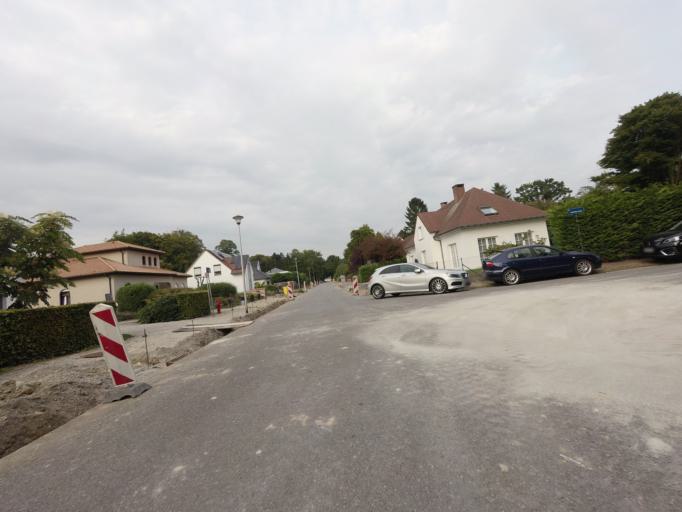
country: BE
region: Flanders
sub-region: Provincie Vlaams-Brabant
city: Steenokkerzeel
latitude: 50.9262
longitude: 4.5159
